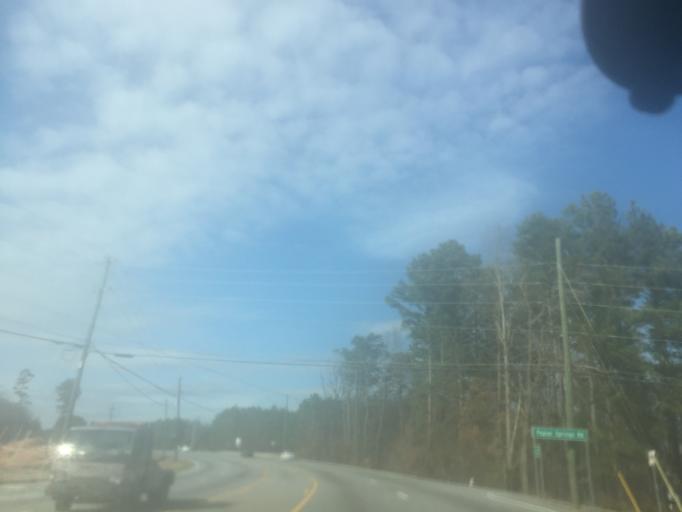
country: US
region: Georgia
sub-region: Clayton County
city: Riverdale
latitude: 33.5867
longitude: -84.4216
